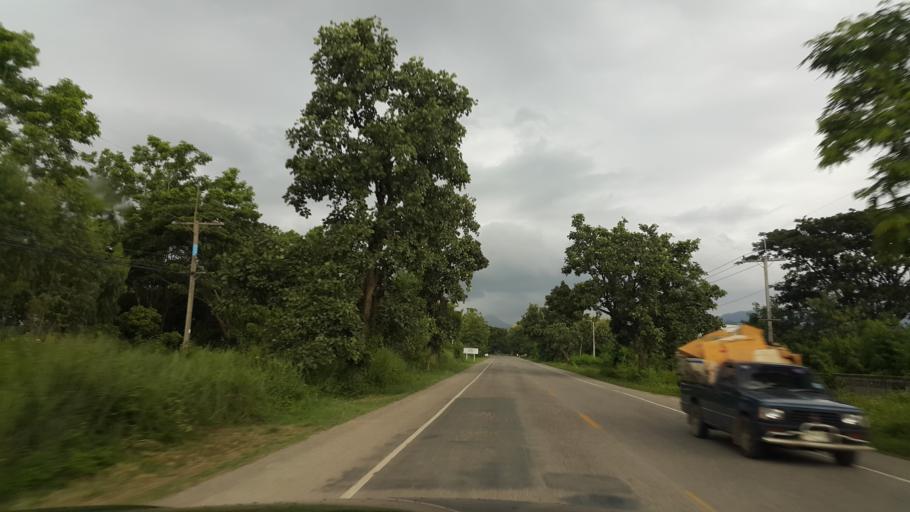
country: TH
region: Phayao
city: Dok Kham Tai
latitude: 19.2273
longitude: 100.0468
